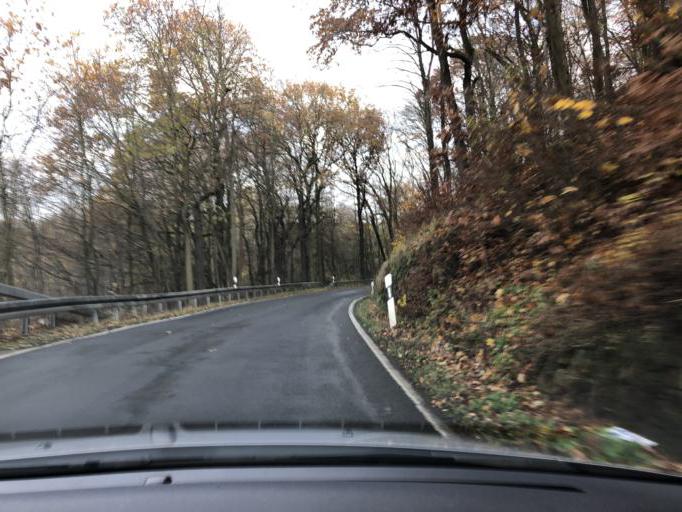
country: DE
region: Saxony
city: Nerchau
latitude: 51.2579
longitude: 12.7849
